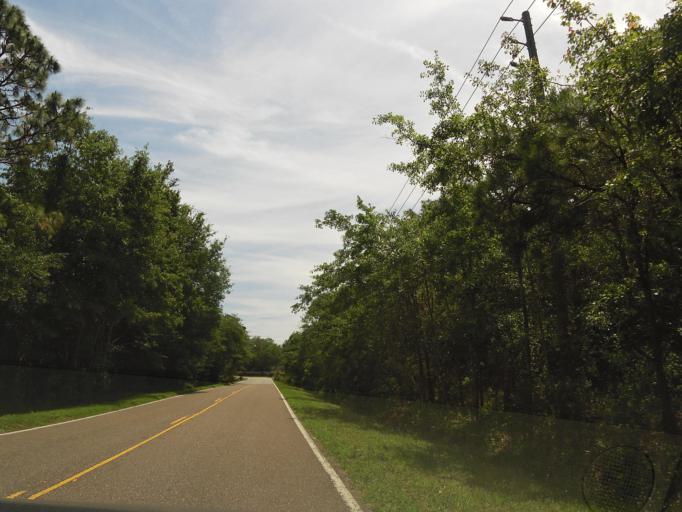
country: US
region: Florida
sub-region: Duval County
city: Jacksonville
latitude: 30.4597
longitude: -81.5348
